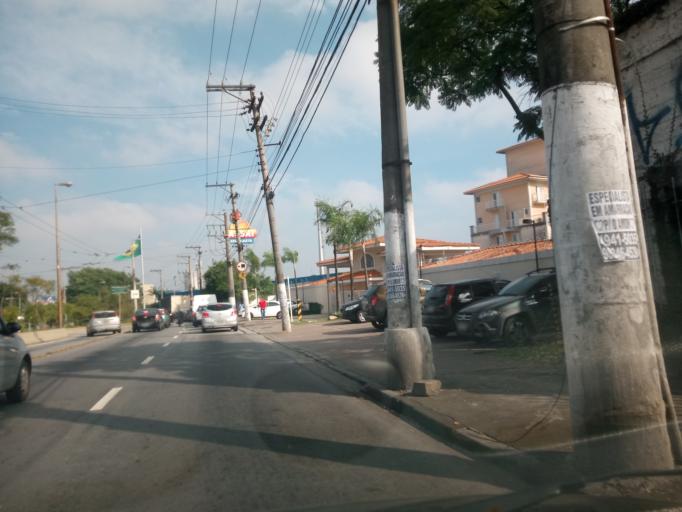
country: BR
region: Sao Paulo
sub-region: Sao Bernardo Do Campo
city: Sao Bernardo do Campo
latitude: -23.6893
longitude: -46.5718
